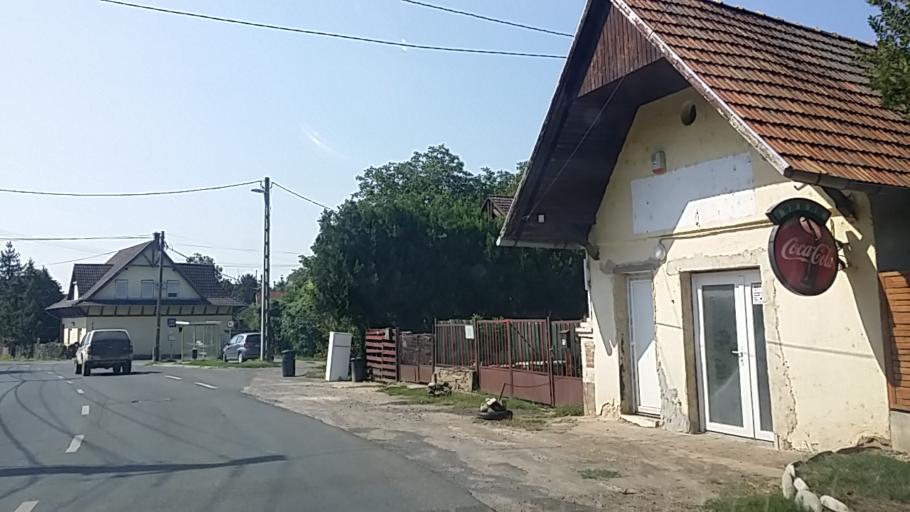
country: HU
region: Baranya
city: Pecs
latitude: 46.0891
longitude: 18.1862
